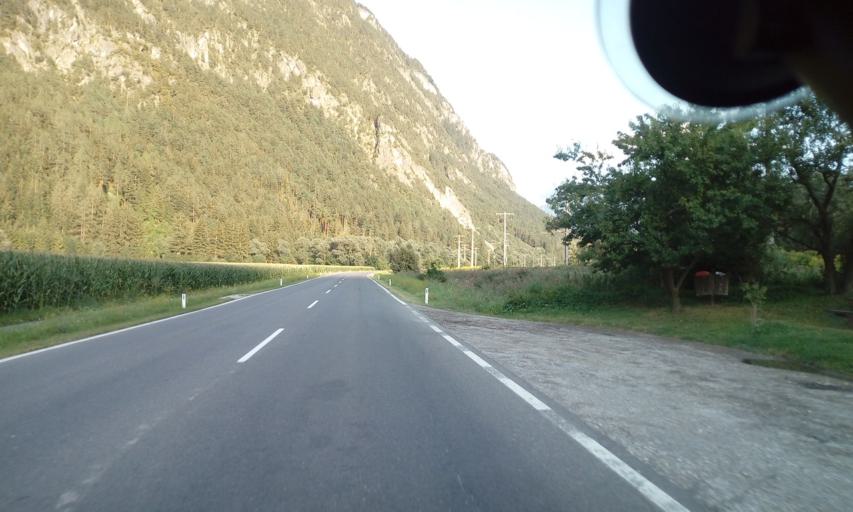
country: AT
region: Tyrol
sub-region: Politischer Bezirk Lienz
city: Nikolsdorf
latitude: 46.7669
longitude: 12.9266
